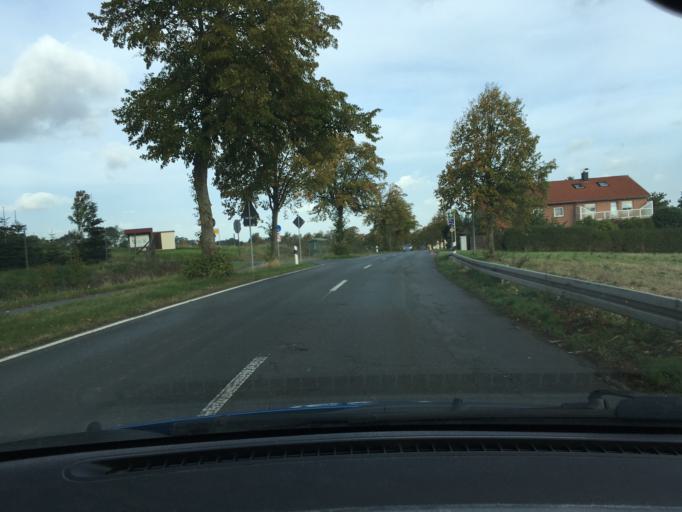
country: DE
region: Lower Saxony
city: Barsinghausen
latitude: 52.3111
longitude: 9.4416
